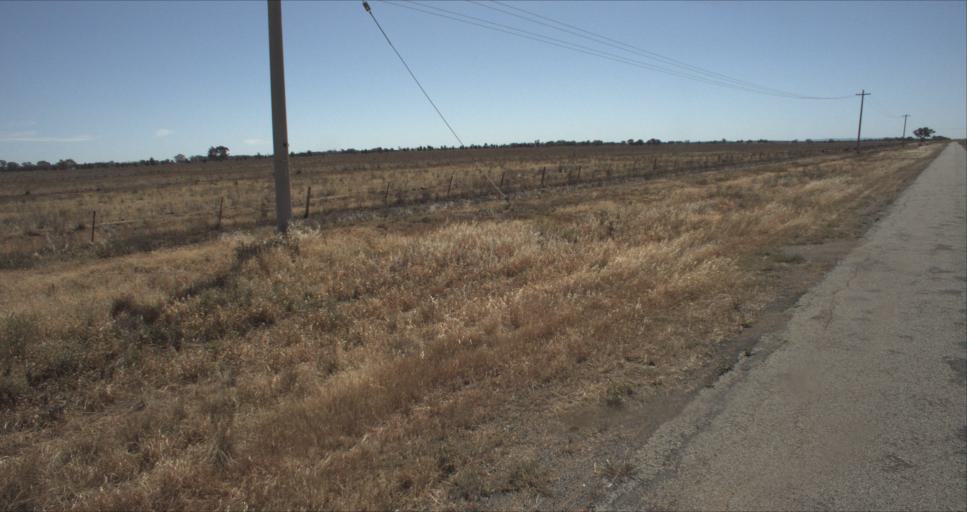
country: AU
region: New South Wales
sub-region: Leeton
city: Leeton
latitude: -34.5076
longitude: 146.3446
